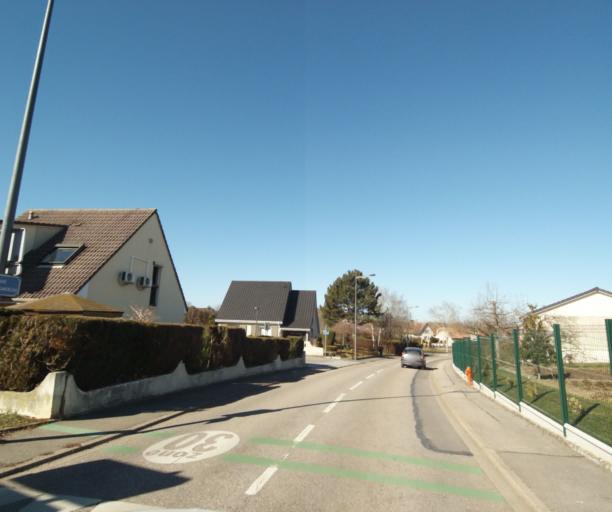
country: FR
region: Lorraine
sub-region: Departement de Meurthe-et-Moselle
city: Heillecourt
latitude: 48.6449
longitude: 6.2063
